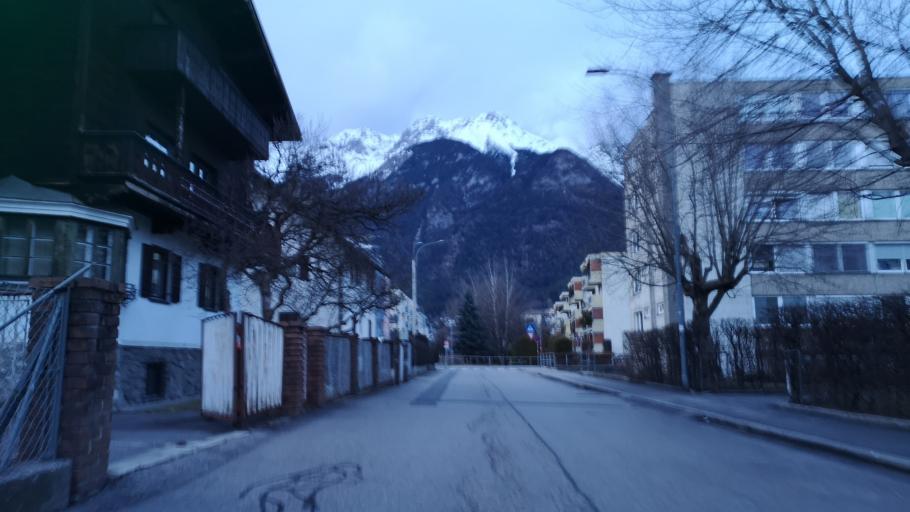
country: AT
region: Tyrol
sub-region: Politischer Bezirk Innsbruck Land
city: Natters
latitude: 47.2565
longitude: 11.3675
